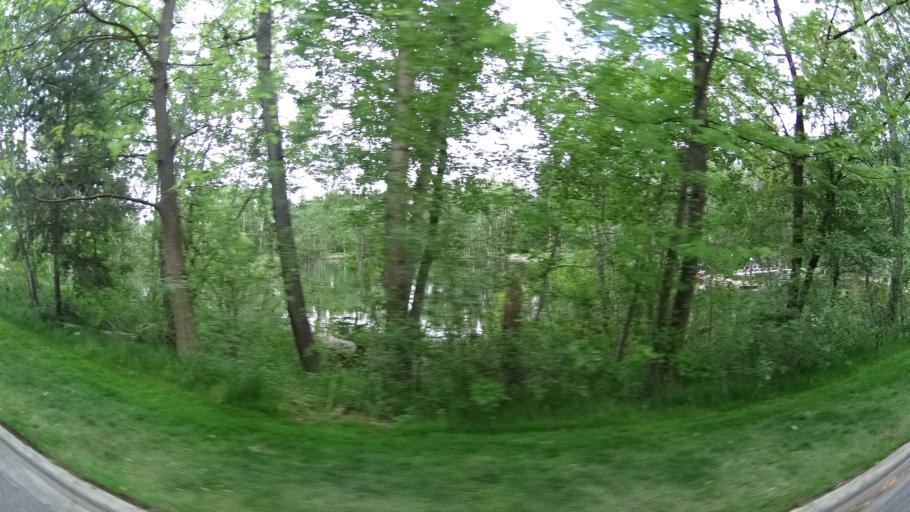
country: US
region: Idaho
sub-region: Ada County
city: Garden City
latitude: 43.6633
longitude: -116.2815
